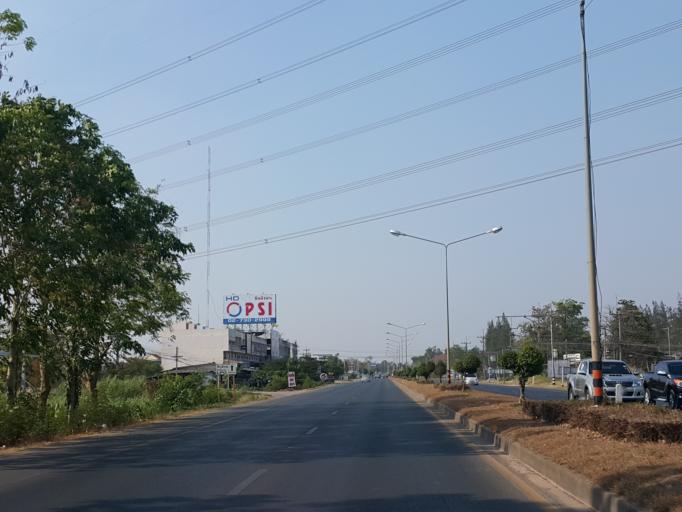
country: TH
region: Phitsanulok
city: Phitsanulok
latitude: 16.8229
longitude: 100.3311
